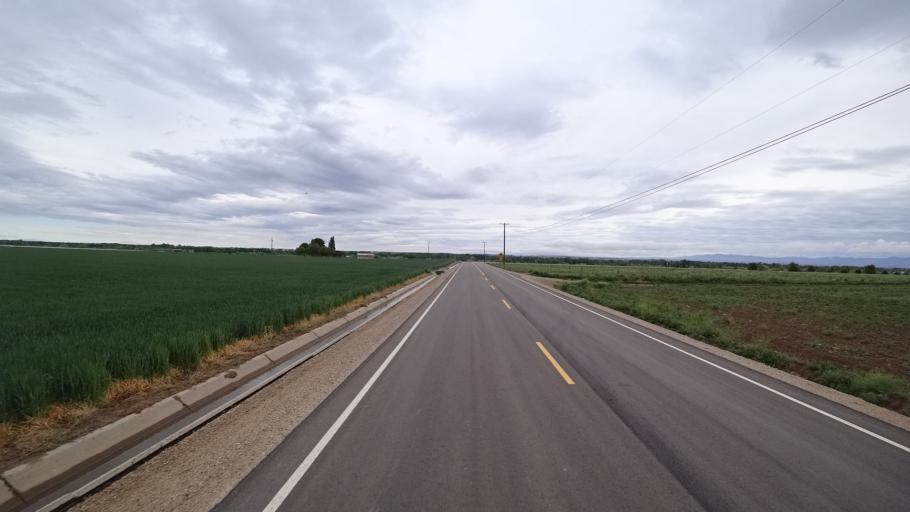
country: US
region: Idaho
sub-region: Ada County
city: Star
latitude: 43.6690
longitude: -116.5129
